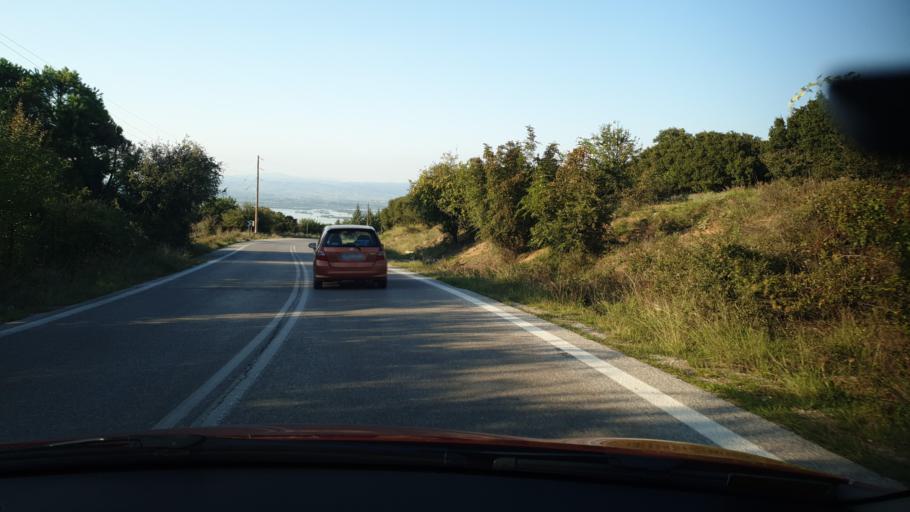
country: GR
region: Central Macedonia
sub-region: Nomos Thessalonikis
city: Agios Vasileios
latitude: 40.6429
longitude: 23.1117
